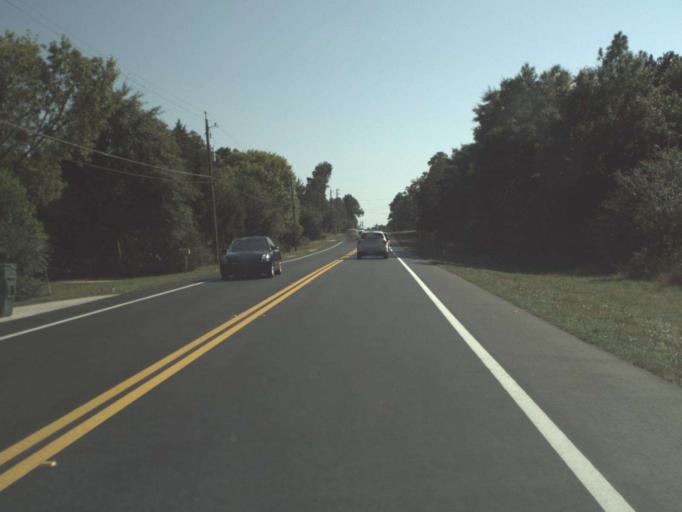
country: US
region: Florida
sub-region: Walton County
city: DeFuniak Springs
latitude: 30.7409
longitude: -86.1482
